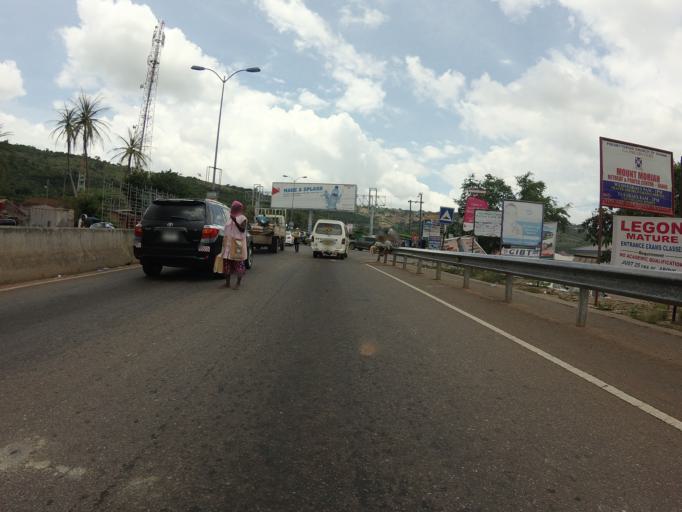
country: GH
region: Eastern
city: Aburi
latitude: 5.7844
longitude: -0.1823
